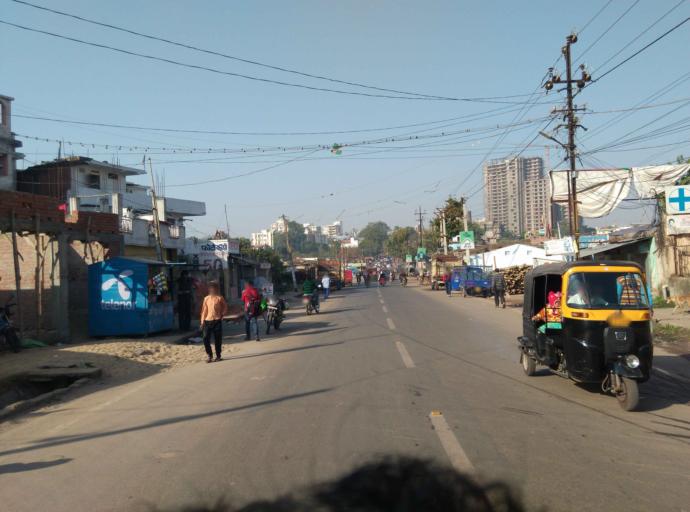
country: IN
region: Jharkhand
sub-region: Ranchi
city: Ranchi
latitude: 23.3745
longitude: 85.3471
